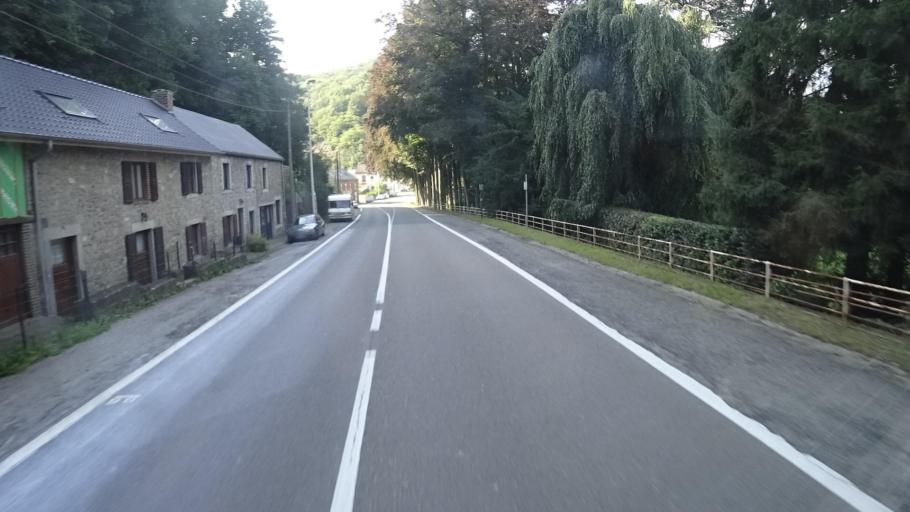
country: BE
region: Wallonia
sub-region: Province de Namur
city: Profondeville
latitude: 50.3594
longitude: 4.8714
